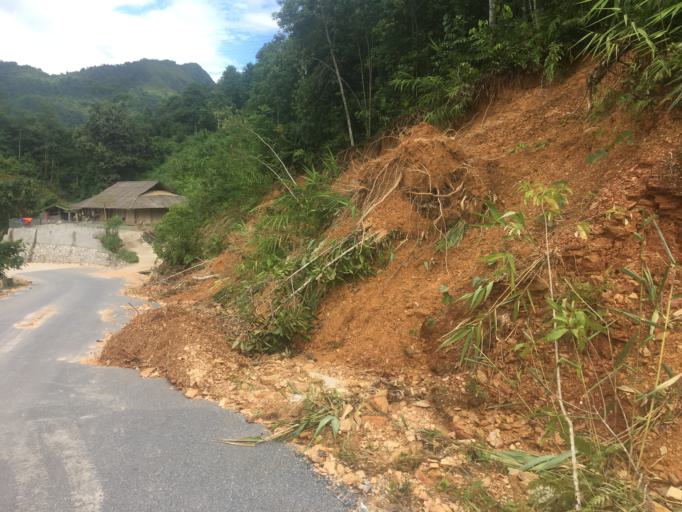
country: VN
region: Ha Giang
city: Thanh Pho Ha Giang
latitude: 22.8559
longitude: 105.0405
